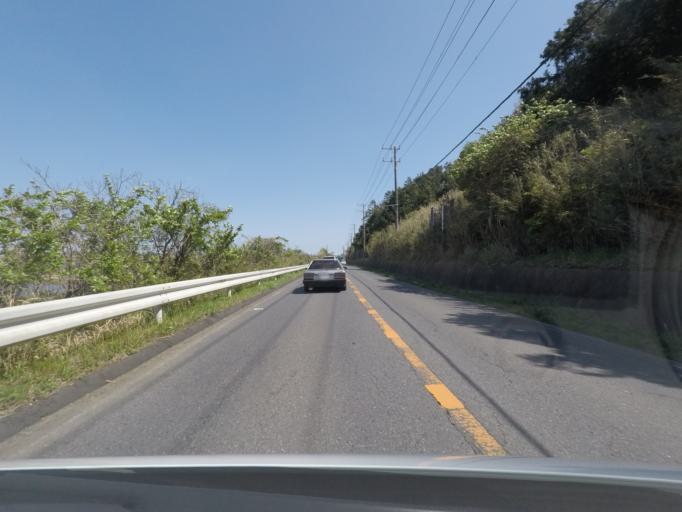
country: JP
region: Chiba
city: Omigawa
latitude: 35.8462
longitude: 140.6418
